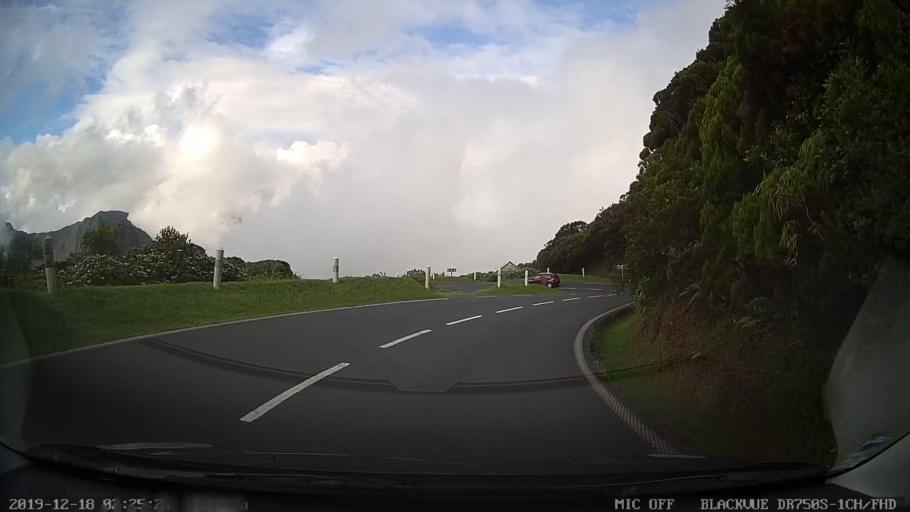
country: RE
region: Reunion
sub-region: Reunion
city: Cilaos
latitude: -21.1625
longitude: 55.6019
